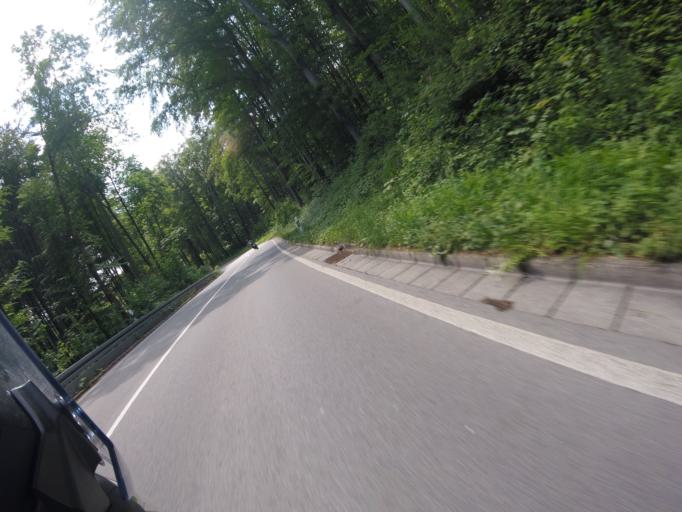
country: DE
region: Bavaria
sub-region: Upper Bavaria
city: Schaftlarn
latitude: 47.9860
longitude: 11.4622
